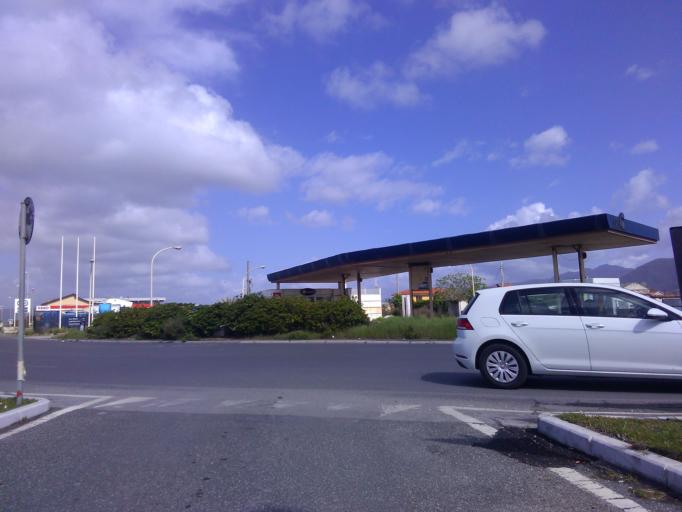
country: IT
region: Tuscany
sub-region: Provincia di Massa-Carrara
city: Marina di Carrara
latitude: 44.0324
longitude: 10.0535
